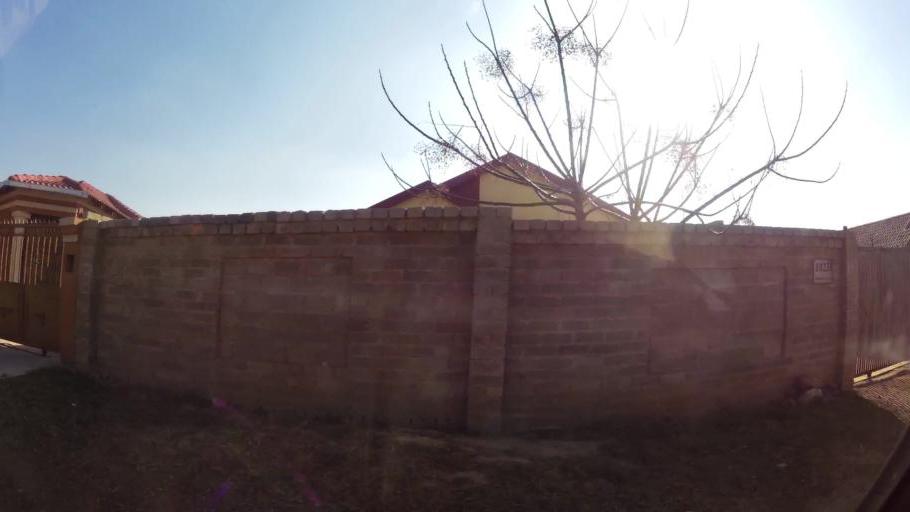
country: ZA
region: Gauteng
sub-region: West Rand District Municipality
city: Muldersdriseloop
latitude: -26.0406
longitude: 27.9110
